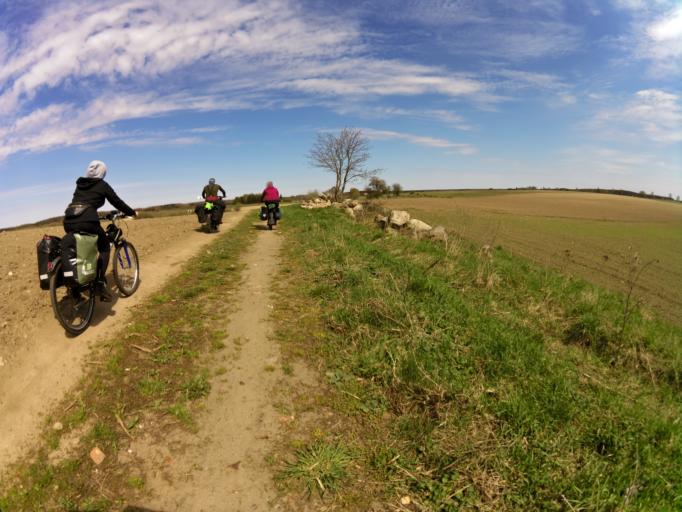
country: PL
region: West Pomeranian Voivodeship
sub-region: Powiat szczecinecki
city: Szczecinek
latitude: 53.7693
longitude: 16.6239
